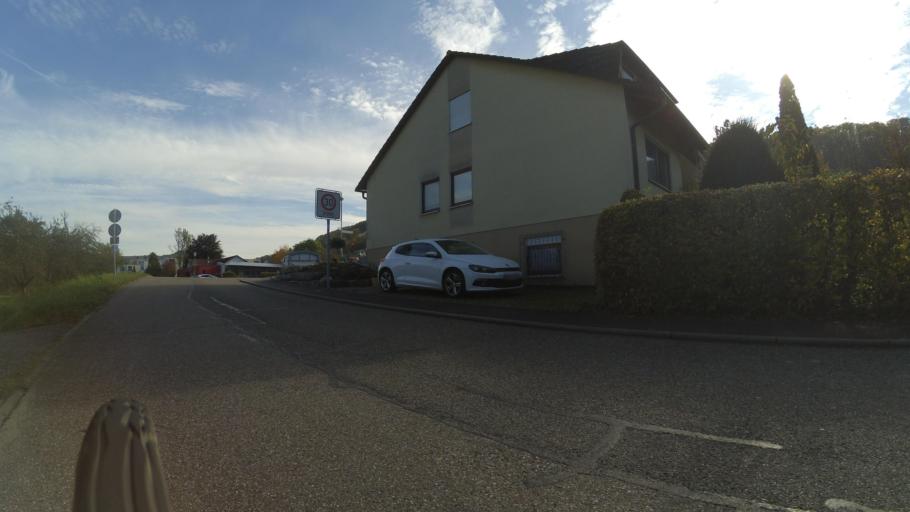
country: DE
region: Baden-Wuerttemberg
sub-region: Regierungsbezirk Stuttgart
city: Ingelfingen
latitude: 49.2976
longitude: 9.6485
